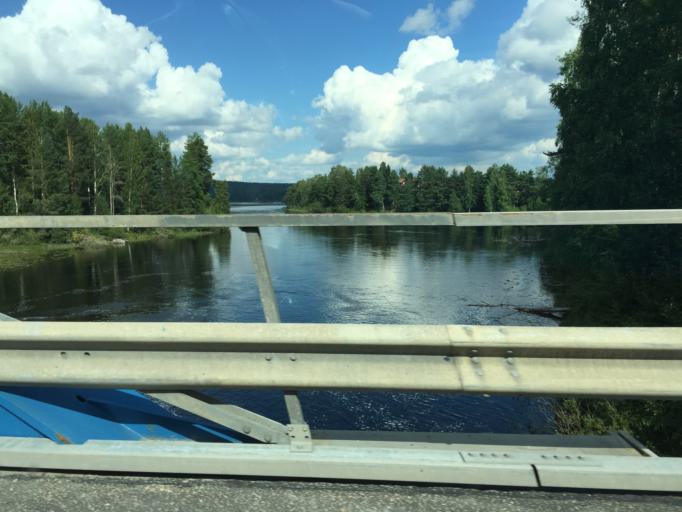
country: SE
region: Gaevleborg
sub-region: Bollnas Kommun
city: Bollnas
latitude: 61.3154
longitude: 16.4400
